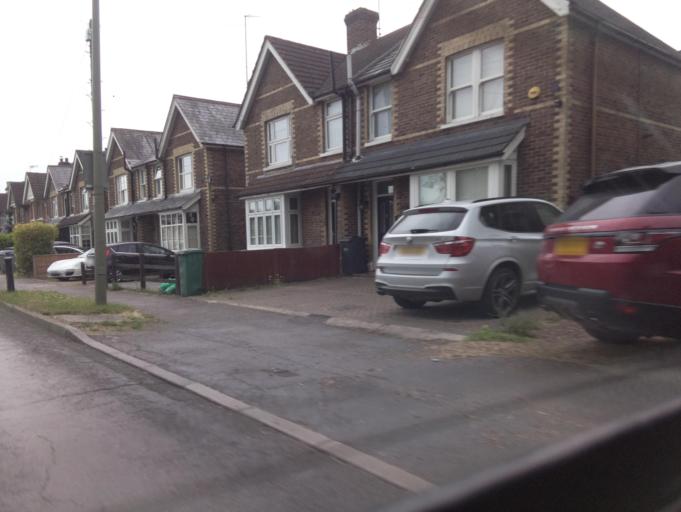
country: GB
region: England
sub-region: Surrey
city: Horley
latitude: 51.1703
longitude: -0.1731
